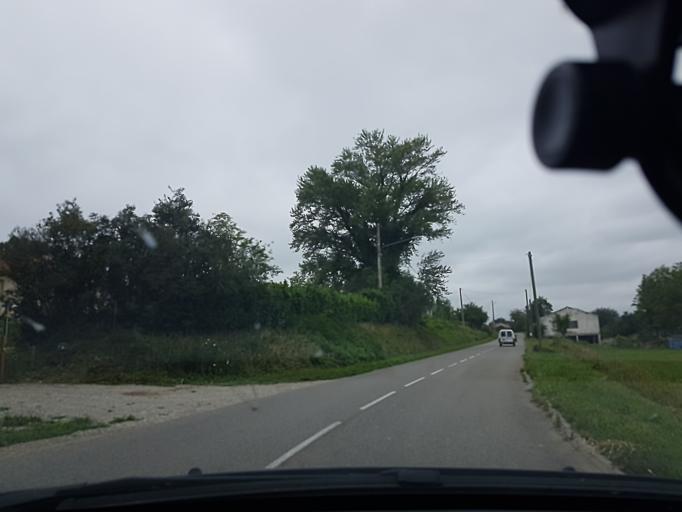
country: FR
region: Midi-Pyrenees
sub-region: Departement de l'Ariege
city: Mirepoix
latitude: 43.0785
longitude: 1.7785
